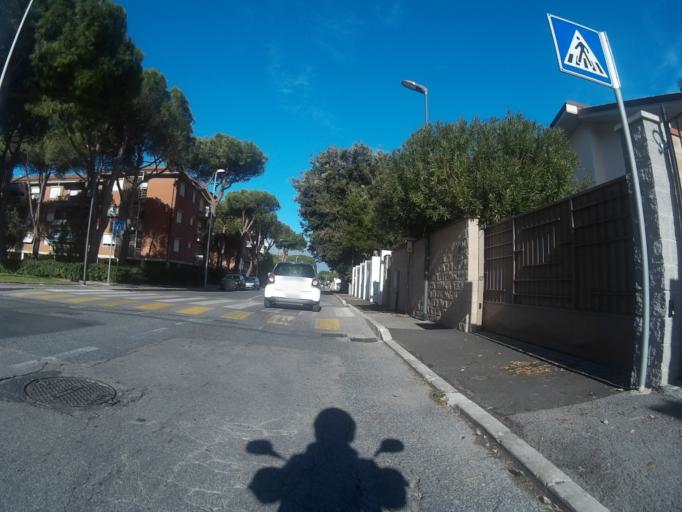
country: IT
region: Tuscany
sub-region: Provincia di Livorno
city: Livorno
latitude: 43.5377
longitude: 10.3417
